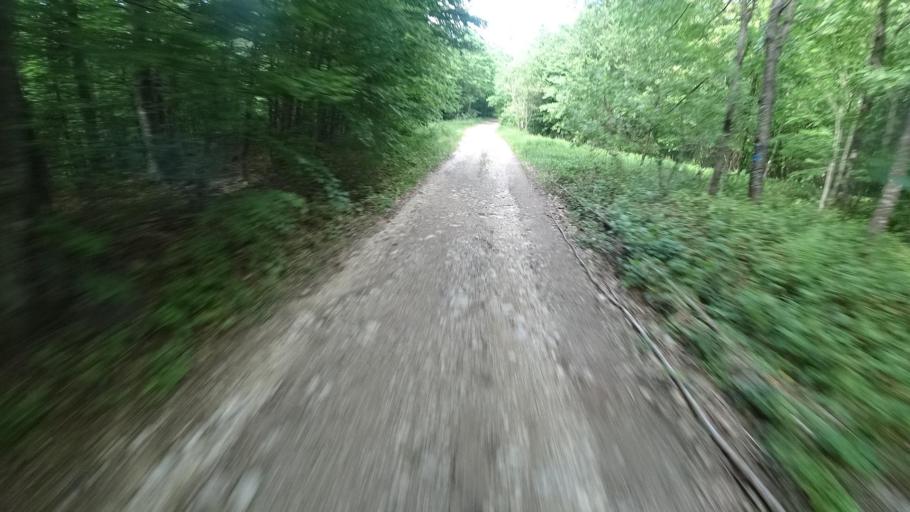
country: BA
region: Federation of Bosnia and Herzegovina
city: Bosanska Krupa
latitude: 44.7642
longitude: 16.2824
